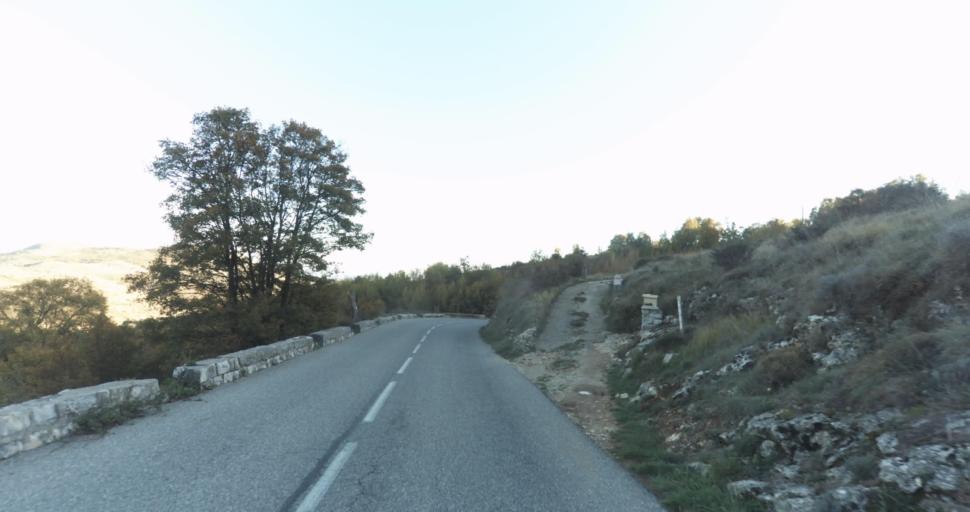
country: FR
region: Provence-Alpes-Cote d'Azur
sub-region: Departement des Alpes-Maritimes
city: Vence
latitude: 43.7571
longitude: 7.0857
